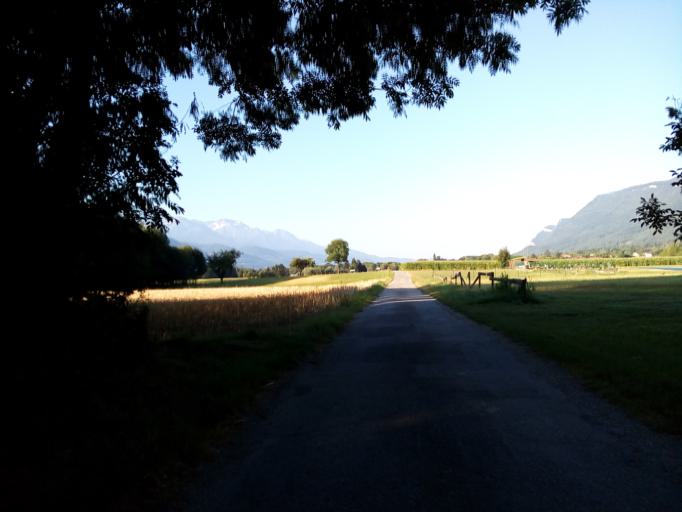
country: FR
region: Rhone-Alpes
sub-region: Departement de l'Isere
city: Le Cheylas
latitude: 45.3883
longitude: 5.9763
